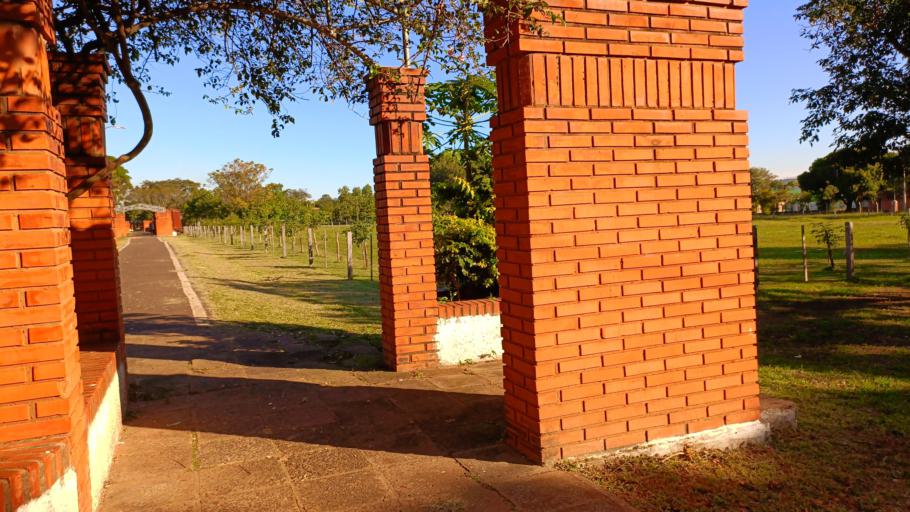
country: PY
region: Itapua
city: Carmen del Parana
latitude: -27.1593
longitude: -56.2404
